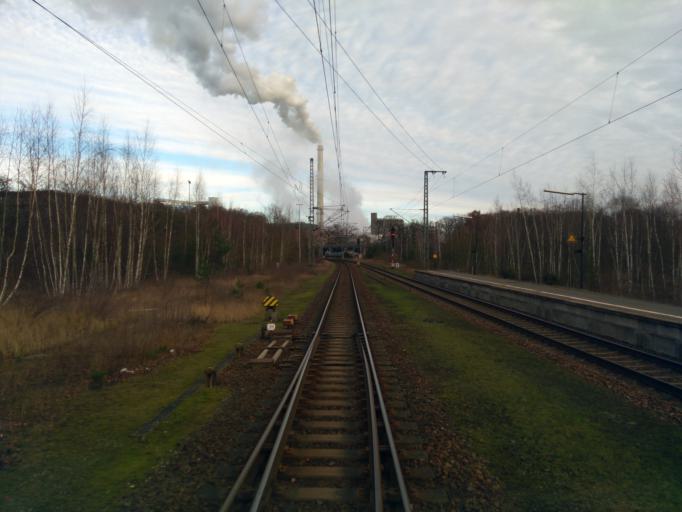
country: DE
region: Lower Saxony
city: Uelzen
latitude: 52.9713
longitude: 10.5539
